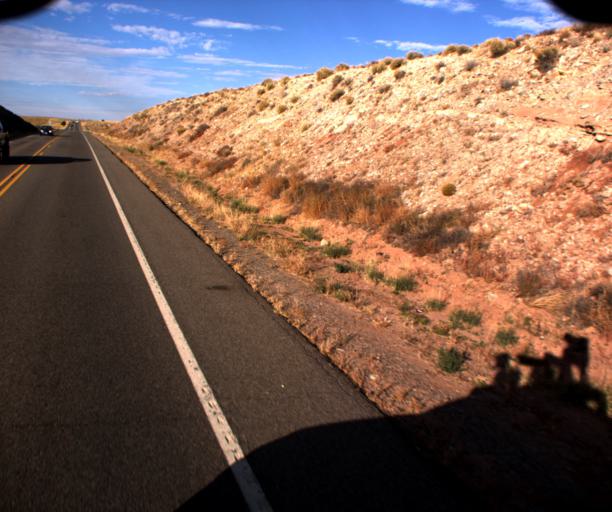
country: US
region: New Mexico
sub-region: San Juan County
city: Shiprock
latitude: 36.9282
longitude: -109.1634
